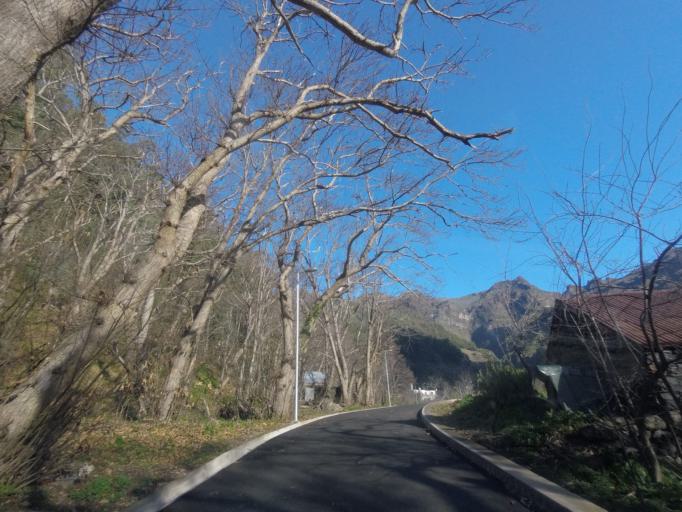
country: PT
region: Madeira
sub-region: Camara de Lobos
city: Curral das Freiras
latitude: 32.7374
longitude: -16.9709
